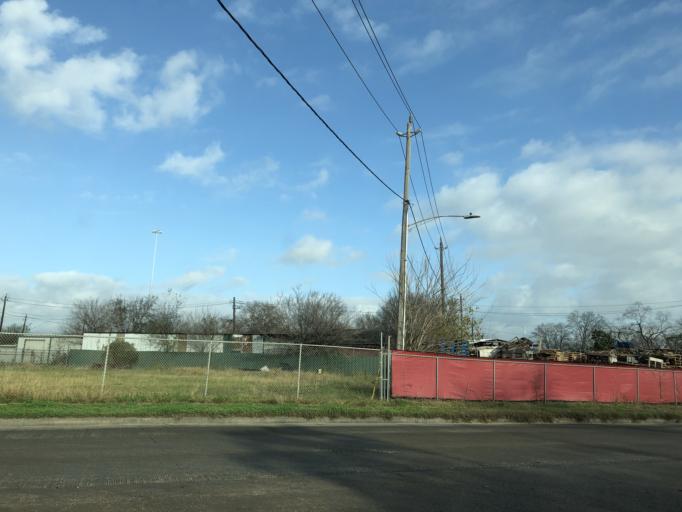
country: US
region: Texas
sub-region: Harris County
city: Jacinto City
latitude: 29.8021
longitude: -95.2856
